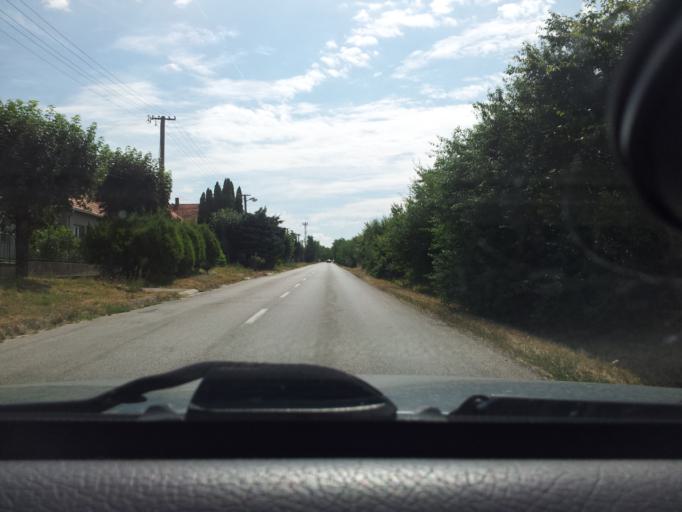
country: SK
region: Nitriansky
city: Zlate Moravce
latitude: 48.3802
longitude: 18.4035
